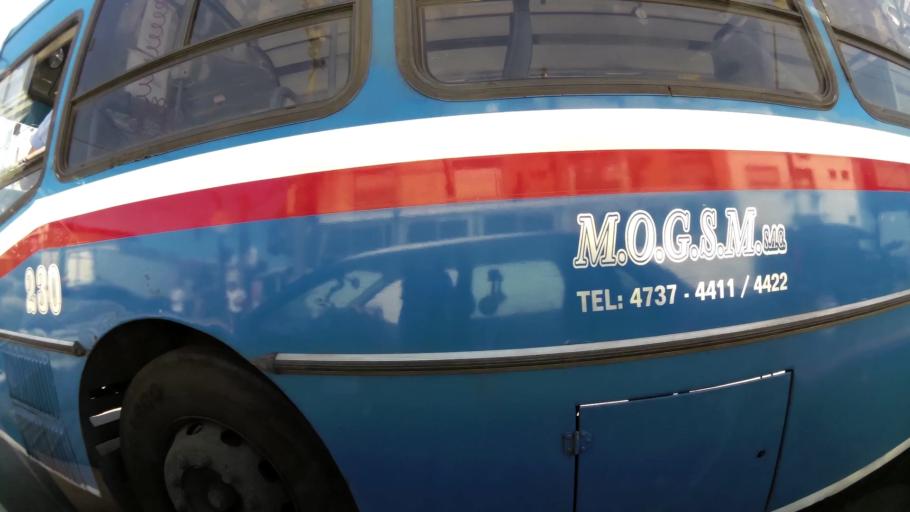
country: AR
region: Buenos Aires
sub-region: Partido de Vicente Lopez
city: Olivos
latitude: -34.5222
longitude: -58.5223
